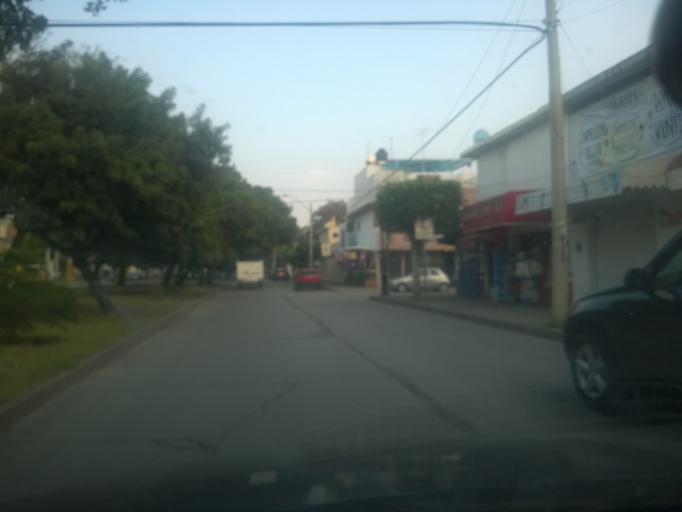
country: MX
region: Guanajuato
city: Leon
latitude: 21.1015
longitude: -101.6512
